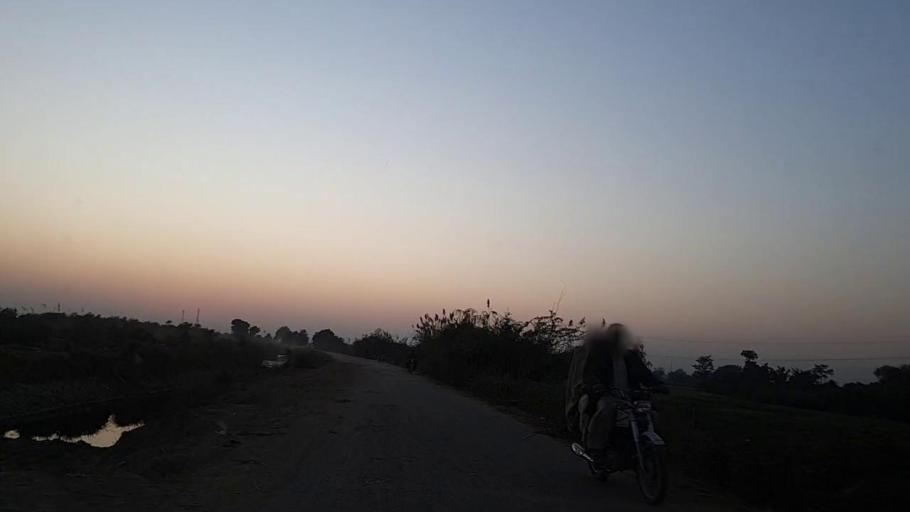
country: PK
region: Sindh
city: Hala
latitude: 25.9602
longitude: 68.3933
